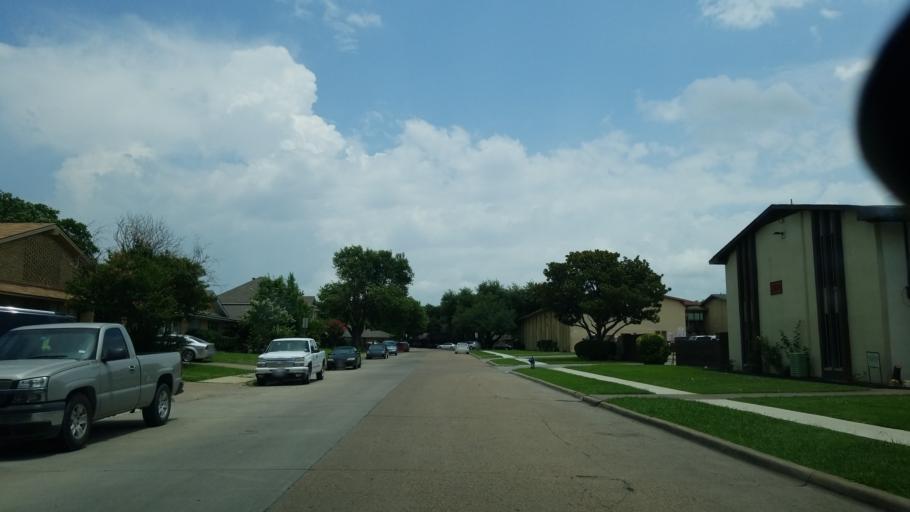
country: US
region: Texas
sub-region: Dallas County
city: Farmers Branch
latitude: 32.8724
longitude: -96.8634
